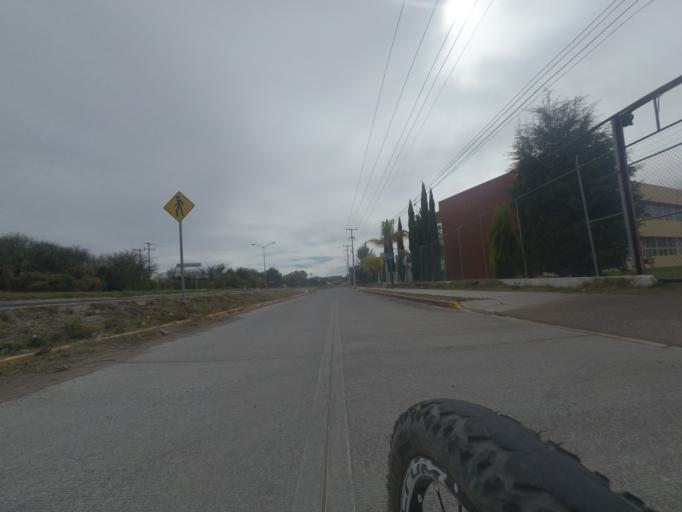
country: MX
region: Aguascalientes
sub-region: Aguascalientes
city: La Loma de los Negritos
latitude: 21.8467
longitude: -102.3533
